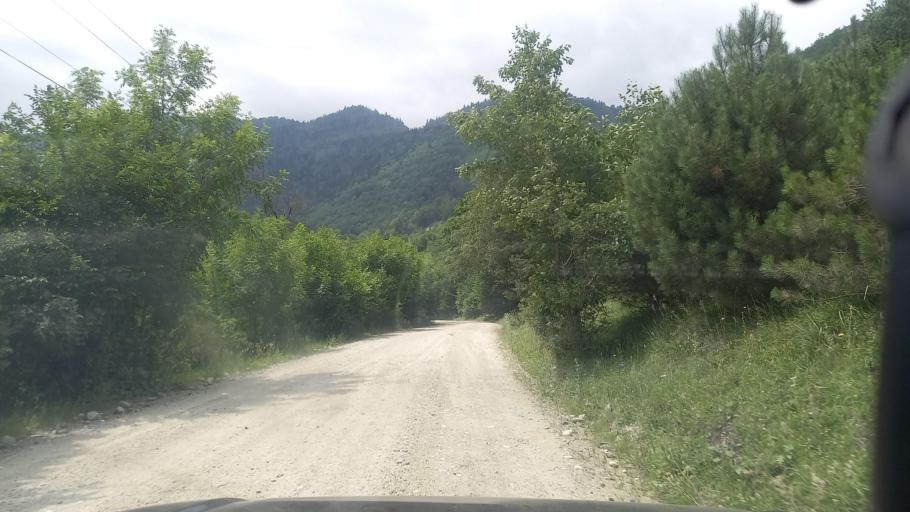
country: RU
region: Karachayevo-Cherkesiya
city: Kurdzhinovo
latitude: 43.9051
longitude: 40.9506
